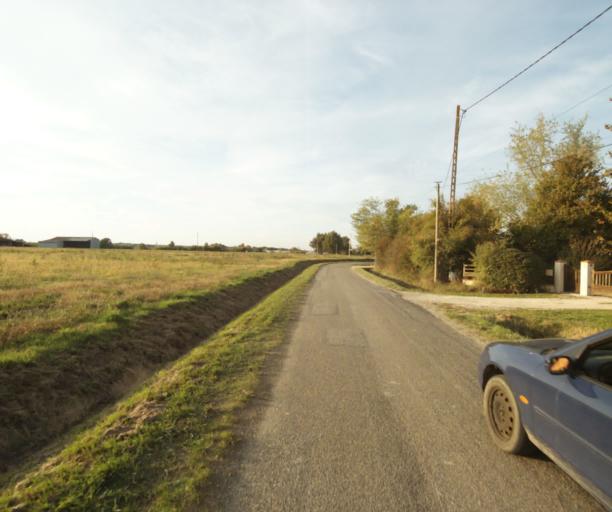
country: FR
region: Midi-Pyrenees
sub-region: Departement du Tarn-et-Garonne
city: Campsas
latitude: 43.8768
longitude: 1.3495
